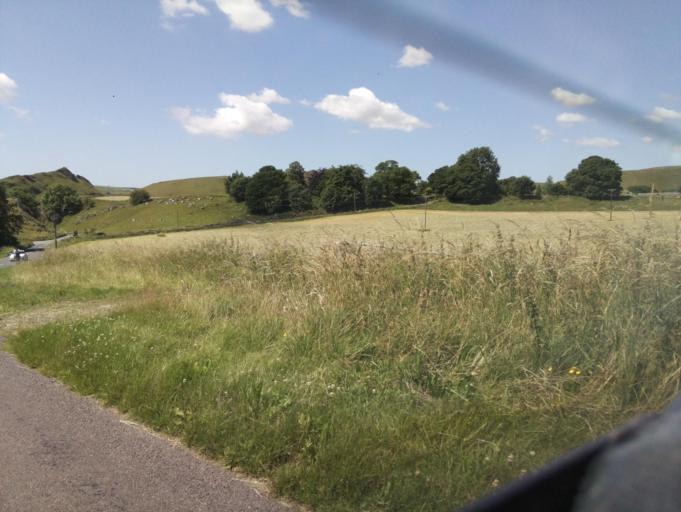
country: GB
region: England
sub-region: Derbyshire
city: Buxton
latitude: 53.2036
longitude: -1.8687
